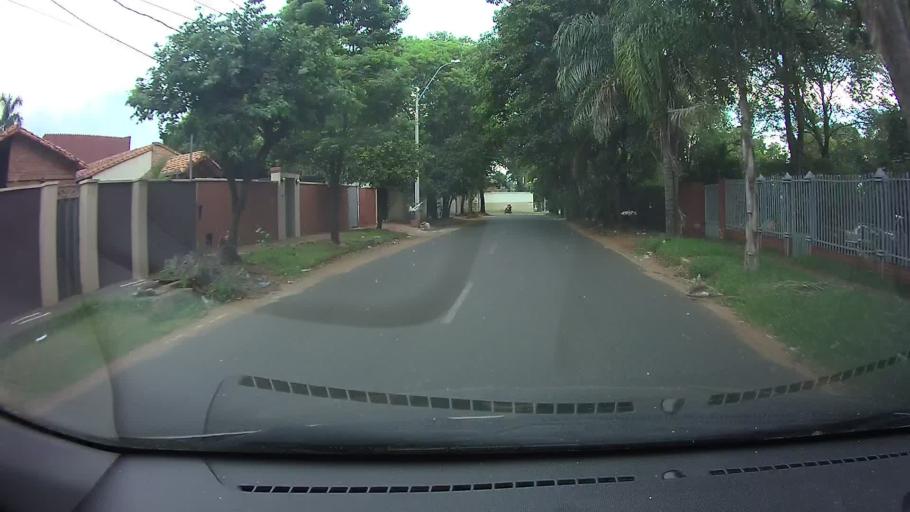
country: PY
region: Central
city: San Lorenzo
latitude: -25.2767
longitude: -57.4938
